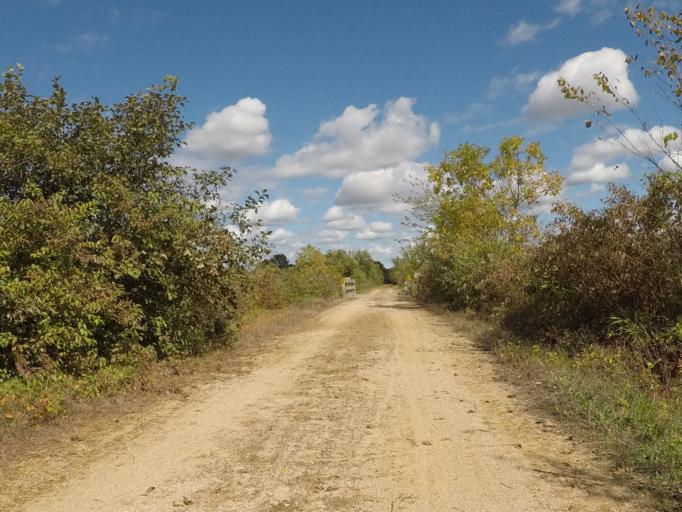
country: US
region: Wisconsin
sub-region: Richland County
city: Richland Center
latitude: 43.2558
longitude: -90.3028
